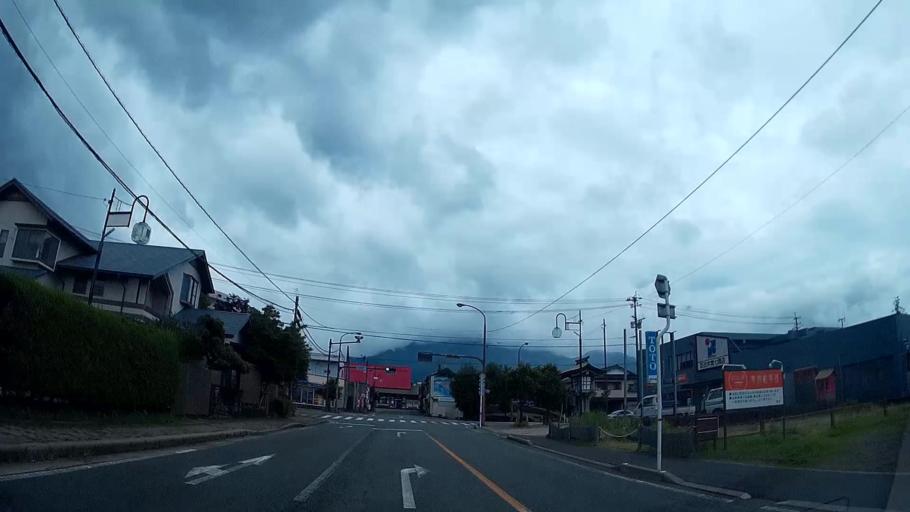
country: JP
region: Kumamoto
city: Aso
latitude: 32.9384
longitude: 131.1178
